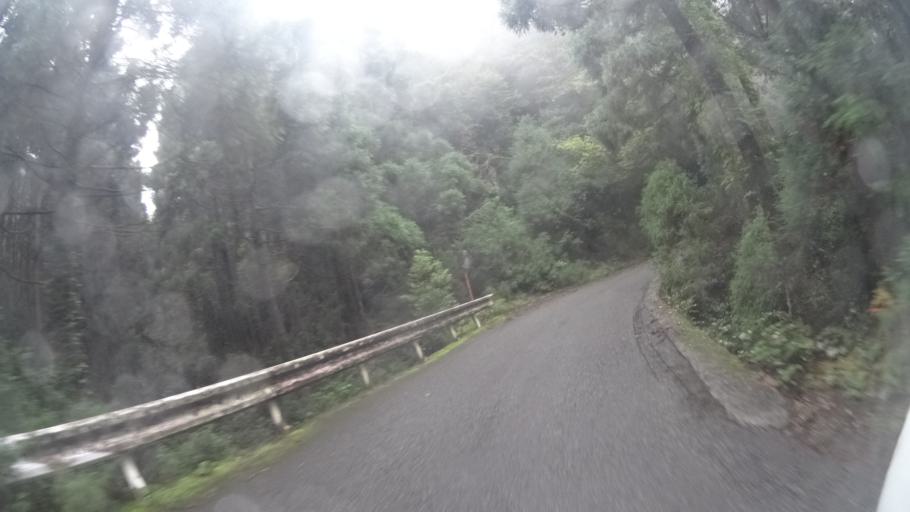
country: JP
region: Kagoshima
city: Nishinoomote
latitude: 30.3005
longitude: 130.5786
